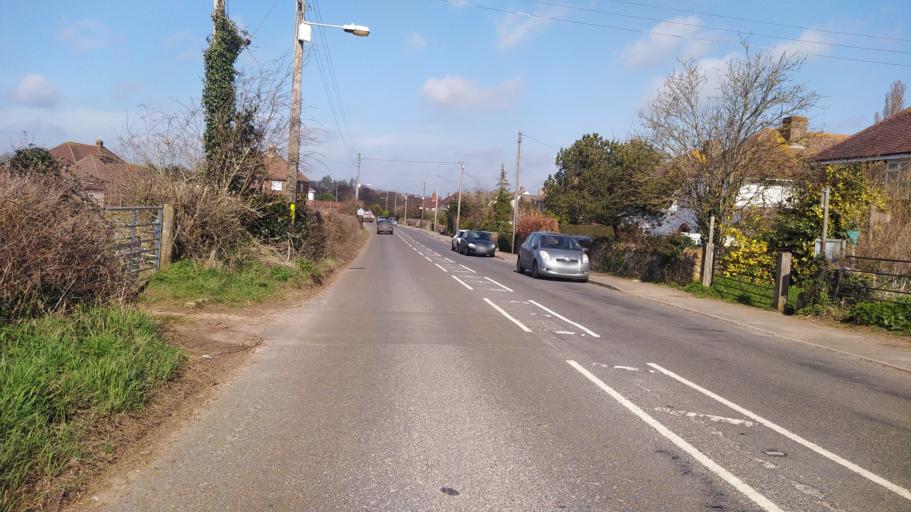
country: GB
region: England
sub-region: Somerset
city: Crewkerne
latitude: 50.8753
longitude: -2.7792
